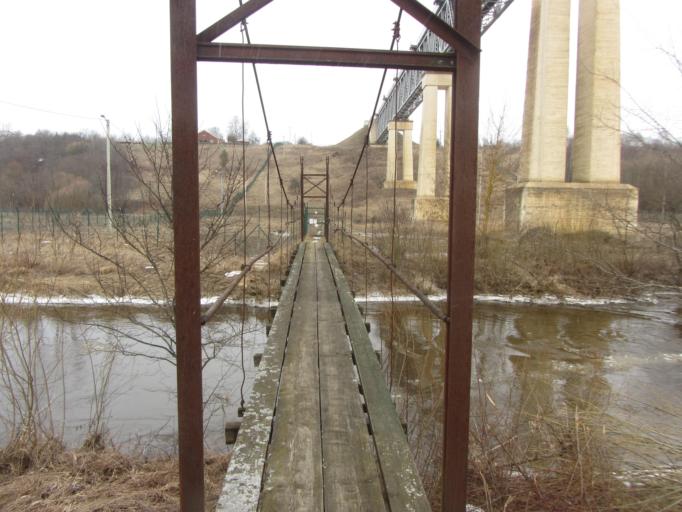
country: LT
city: Raseiniai
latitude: 55.5066
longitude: 23.0865
